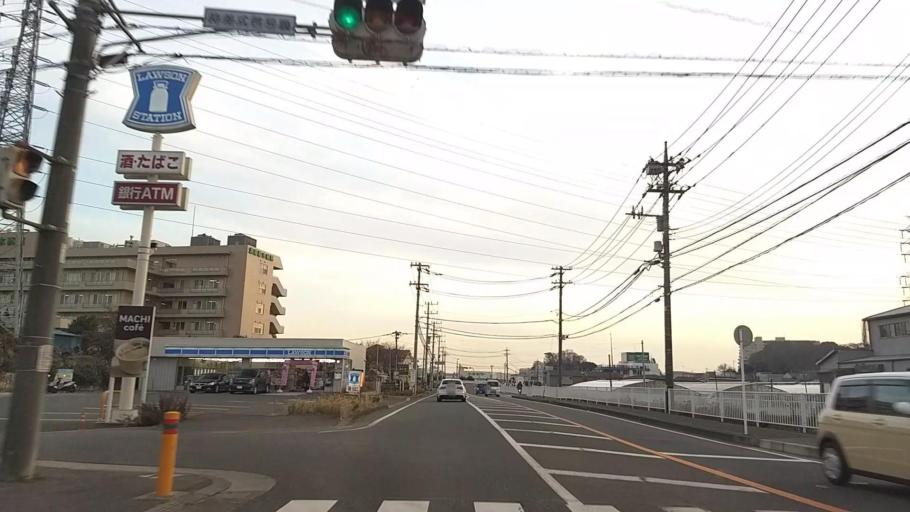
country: JP
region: Kanagawa
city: Atsugi
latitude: 35.4337
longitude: 139.3525
